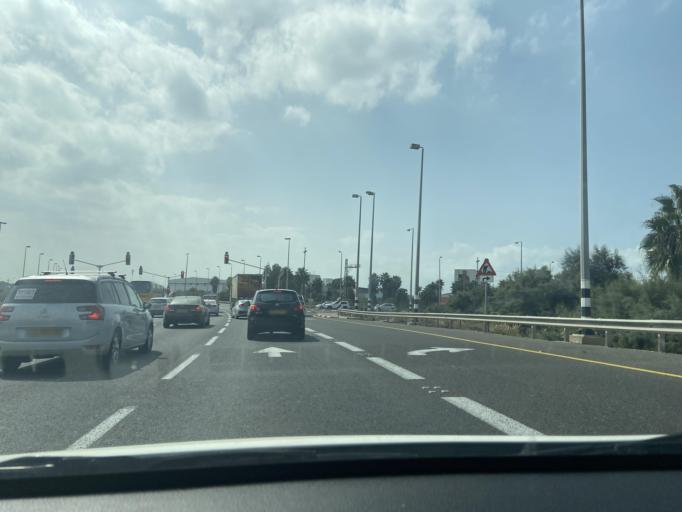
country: IL
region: Northern District
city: `Akko
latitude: 32.9055
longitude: 35.0902
